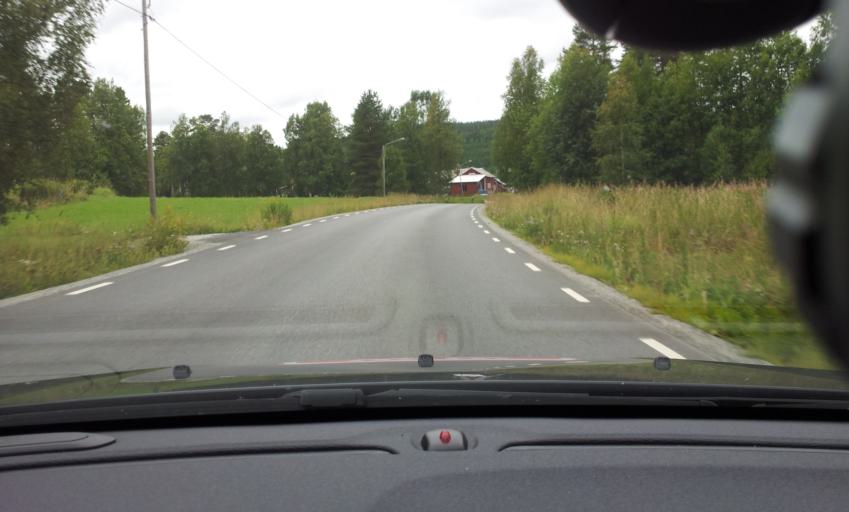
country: SE
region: Jaemtland
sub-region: Braecke Kommun
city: Braecke
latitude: 63.0600
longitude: 15.3400
